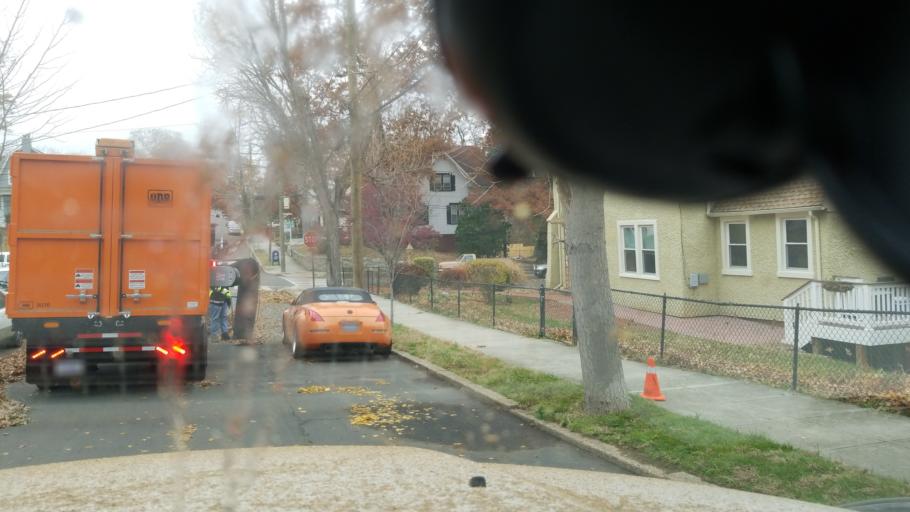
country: US
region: Maryland
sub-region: Prince George's County
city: Mount Rainier
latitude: 38.9304
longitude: -76.9667
